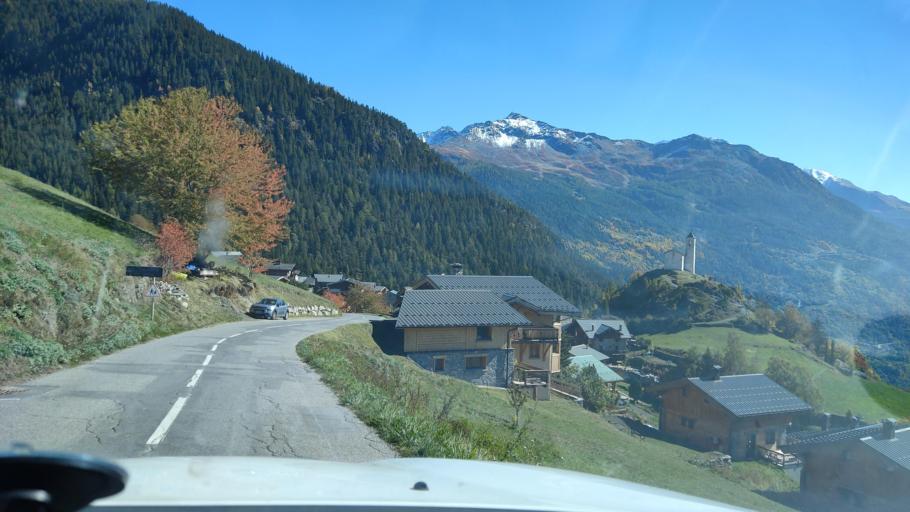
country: FR
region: Rhone-Alpes
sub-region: Departement de la Savoie
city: Seez
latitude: 45.6164
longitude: 6.8599
